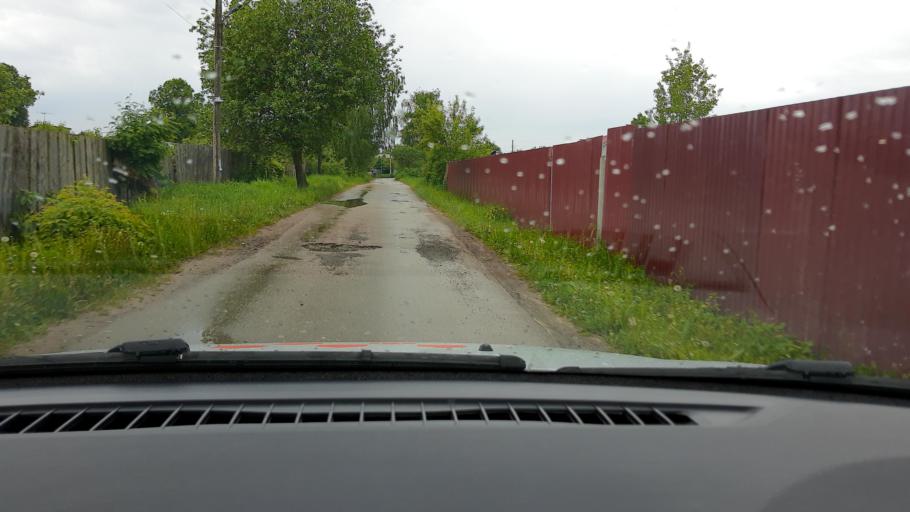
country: RU
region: Nizjnij Novgorod
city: Gorbatovka
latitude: 56.2328
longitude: 43.7153
